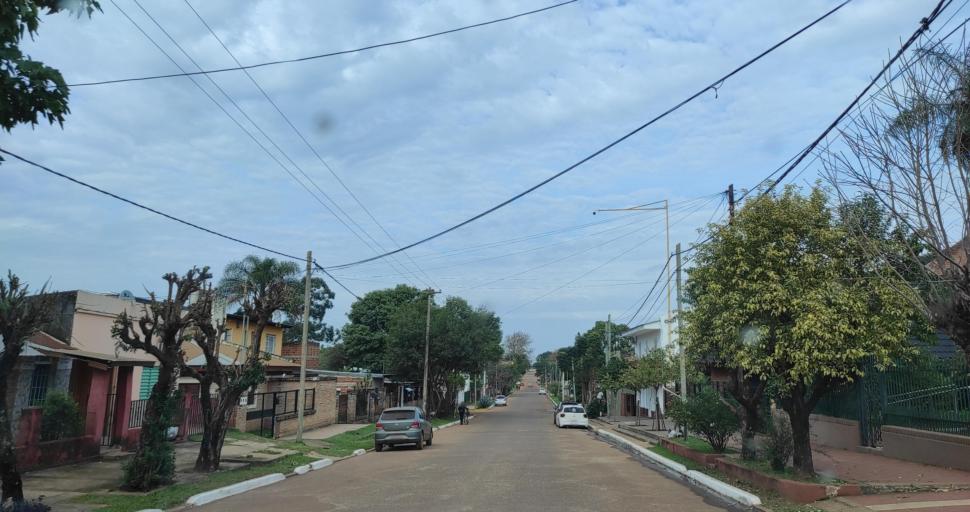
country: AR
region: Corrientes
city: Santo Tome
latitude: -28.5519
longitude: -56.0367
